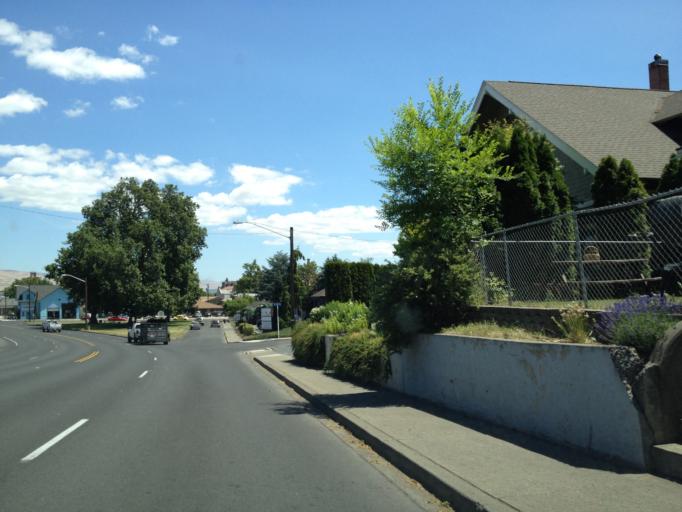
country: US
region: Washington
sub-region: Yakima County
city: Yakima
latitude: 46.5971
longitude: -120.5280
